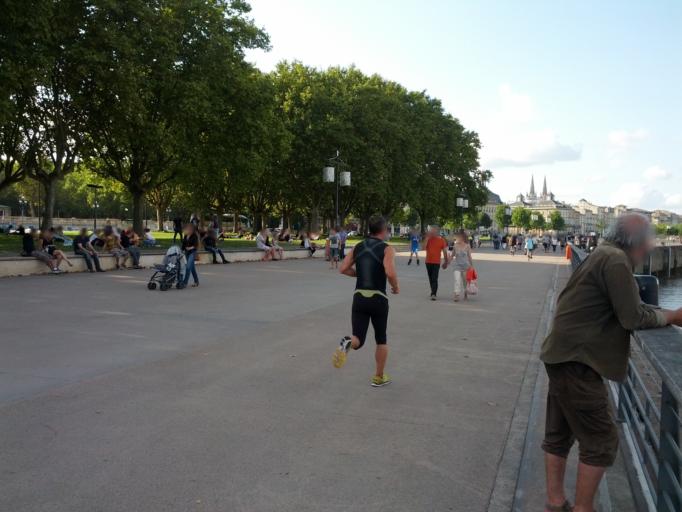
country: FR
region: Aquitaine
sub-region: Departement de la Gironde
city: Bordeaux
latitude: 44.8454
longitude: -0.5698
